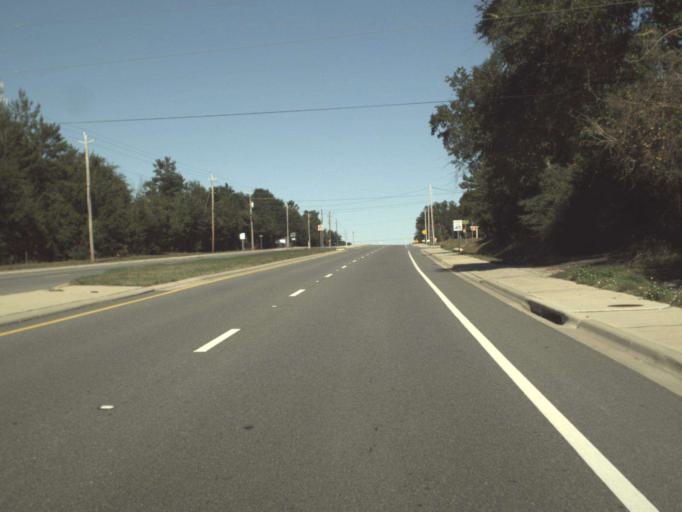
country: US
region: Florida
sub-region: Santa Rosa County
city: Holley
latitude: 30.4641
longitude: -86.9100
